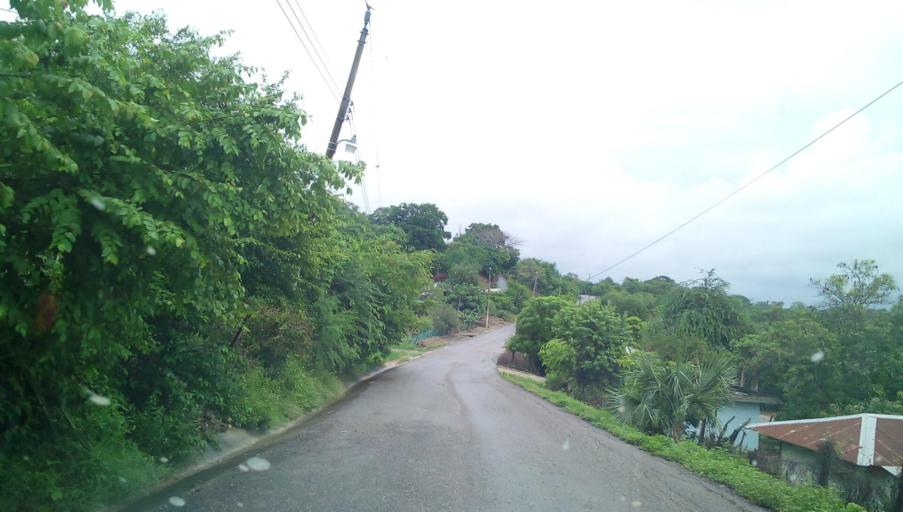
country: MX
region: Veracruz
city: Tempoal de Sanchez
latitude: 21.4619
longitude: -98.4244
